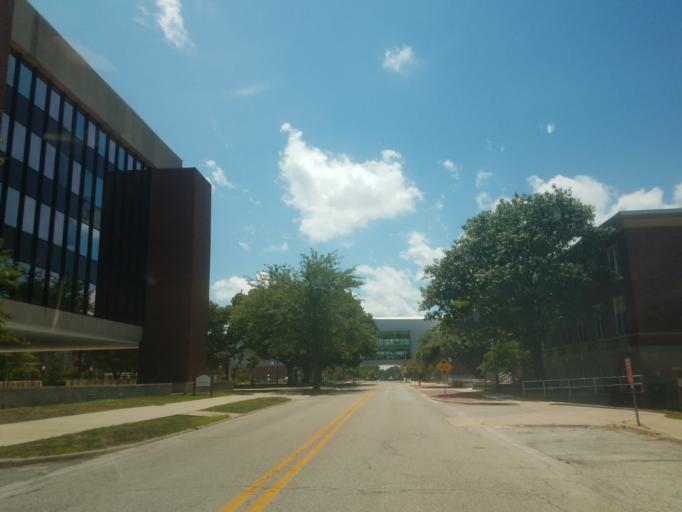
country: US
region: Illinois
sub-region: McLean County
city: Normal
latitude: 40.5092
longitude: -88.9932
